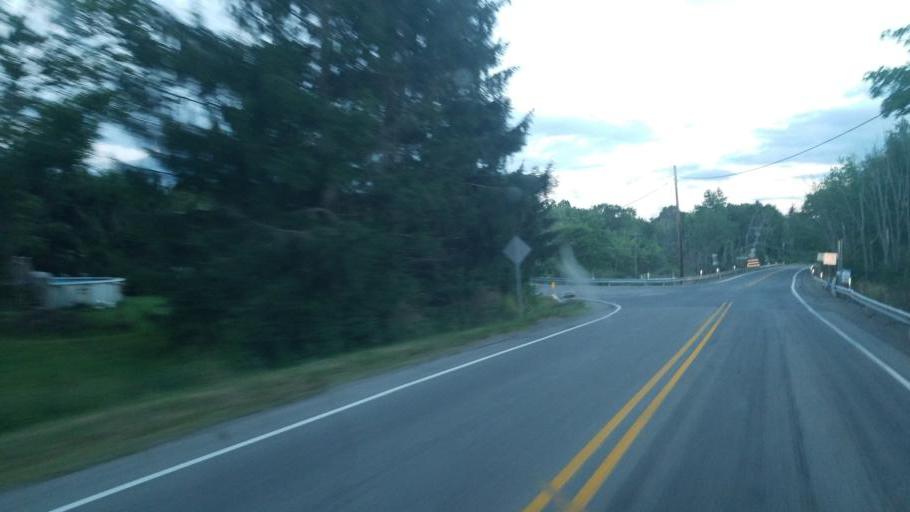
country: US
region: Pennsylvania
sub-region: Clarion County
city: Knox
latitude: 41.1920
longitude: -79.5480
